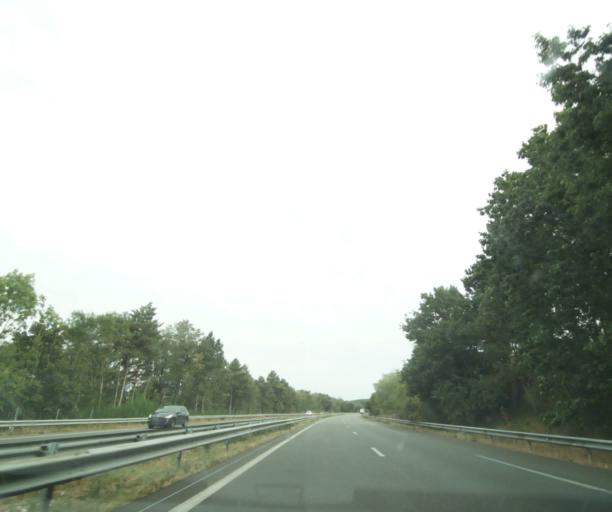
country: FR
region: Aquitaine
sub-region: Departement du Lot-et-Garonne
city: Roquefort
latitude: 44.1765
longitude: 0.5728
